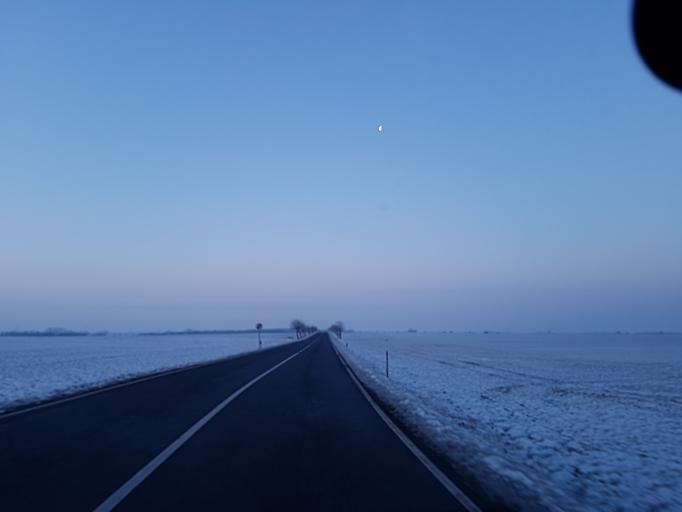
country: DE
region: Saxony
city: Strehla
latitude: 51.3280
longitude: 13.2034
